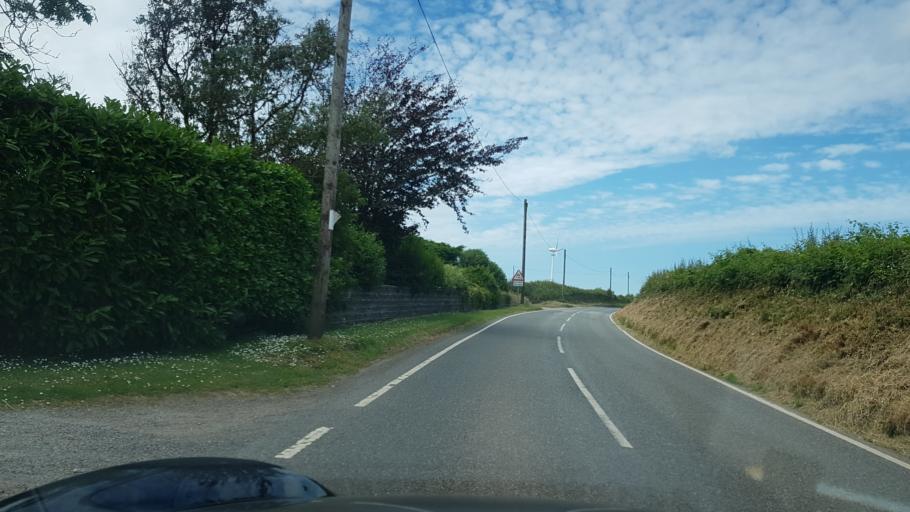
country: GB
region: Wales
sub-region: Carmarthenshire
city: Llanddowror
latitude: 51.7641
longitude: -4.5763
